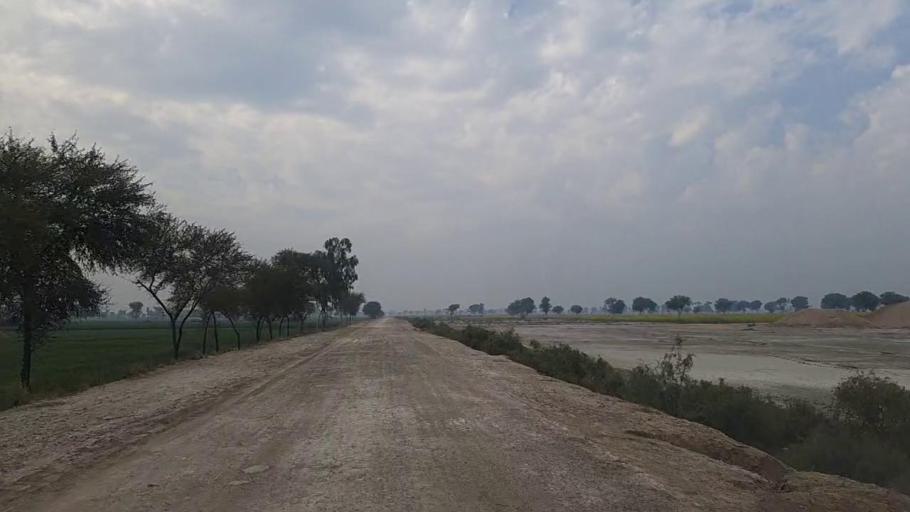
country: PK
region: Sindh
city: Nawabshah
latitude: 26.3654
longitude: 68.3936
